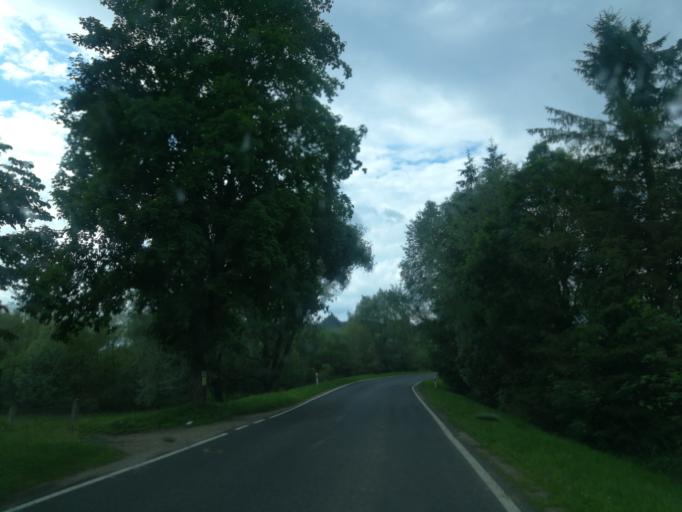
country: PL
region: Subcarpathian Voivodeship
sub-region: Powiat leski
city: Uherce Mineralne
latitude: 49.4617
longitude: 22.4003
